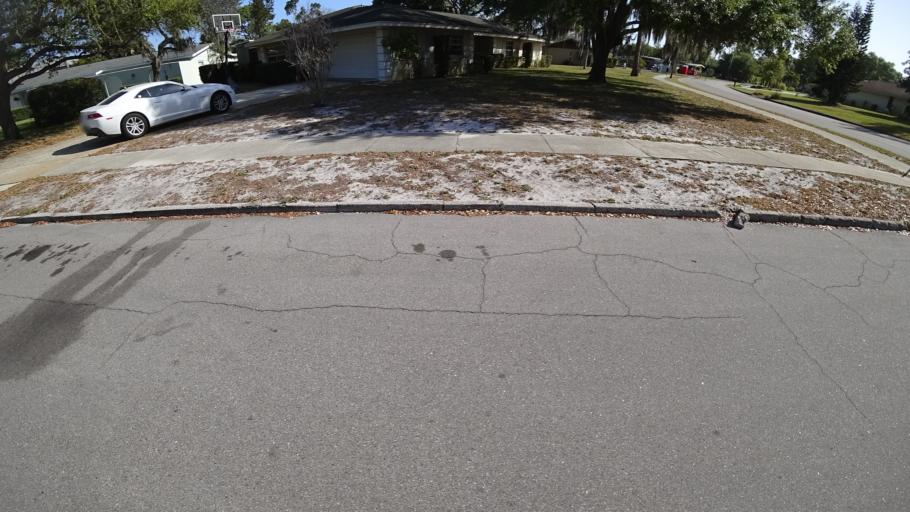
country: US
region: Florida
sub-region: Manatee County
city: Whitfield
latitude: 27.4114
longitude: -82.5676
